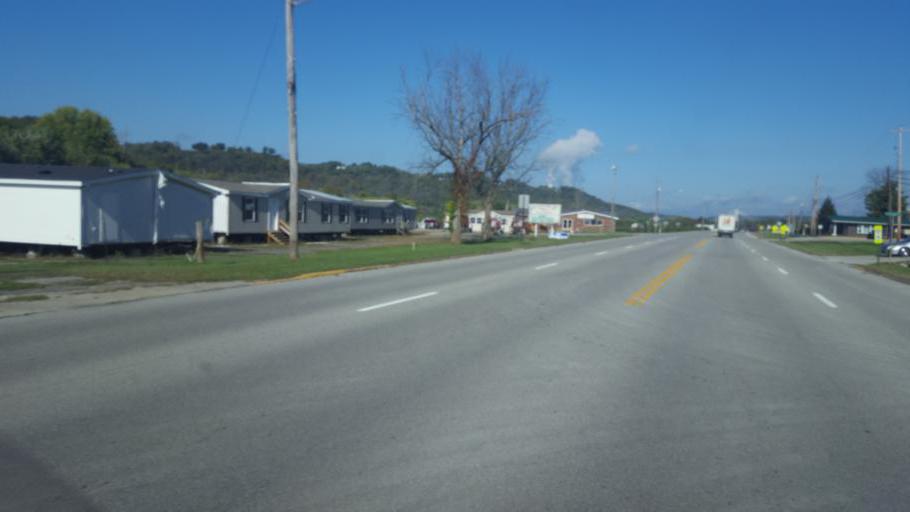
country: US
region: Ohio
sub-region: Brown County
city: Aberdeen
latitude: 38.6614
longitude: -83.7678
